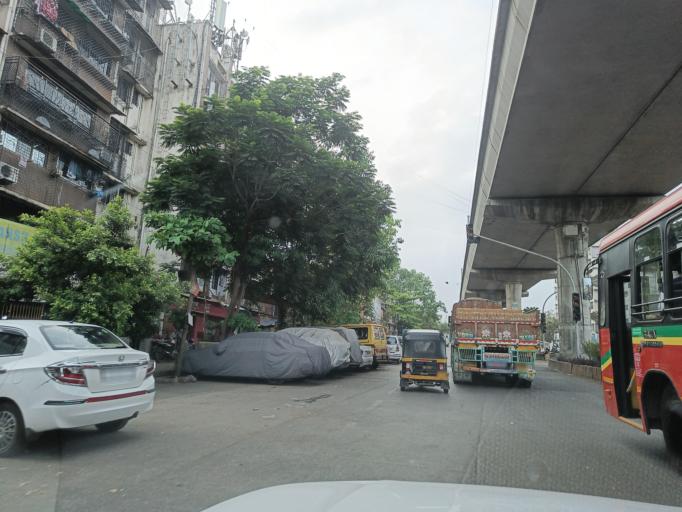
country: IN
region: Maharashtra
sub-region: Mumbai Suburban
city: Powai
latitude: 19.0950
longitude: 72.8973
